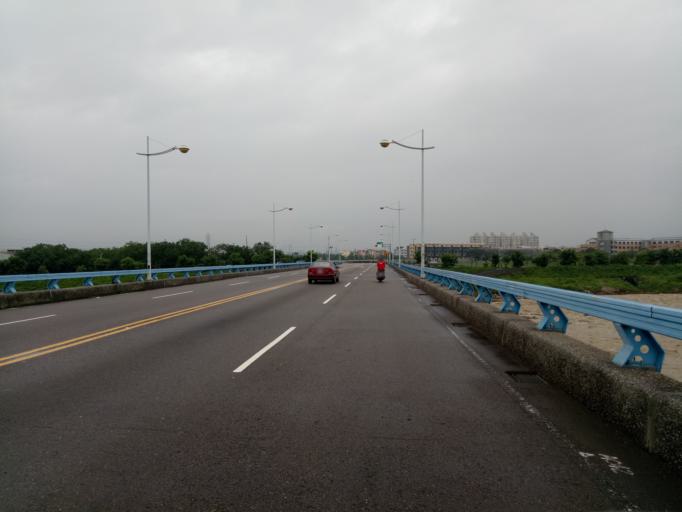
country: TW
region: Taiwan
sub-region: Taichung City
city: Taichung
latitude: 24.1088
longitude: 120.7153
